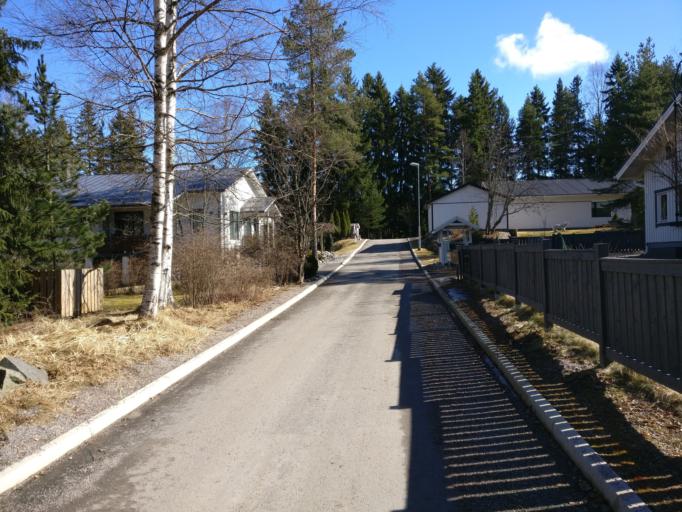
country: FI
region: Uusimaa
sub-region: Helsinki
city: Jaervenpaeae
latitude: 60.4895
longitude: 25.0809
